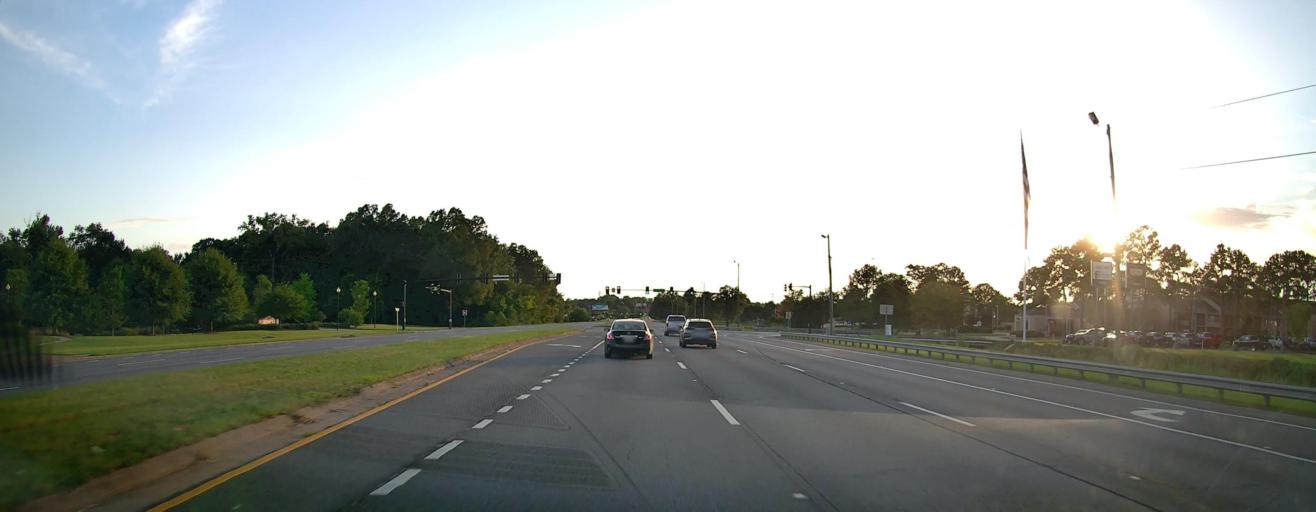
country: US
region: Georgia
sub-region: Muscogee County
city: Columbus
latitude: 32.5090
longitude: -84.9356
